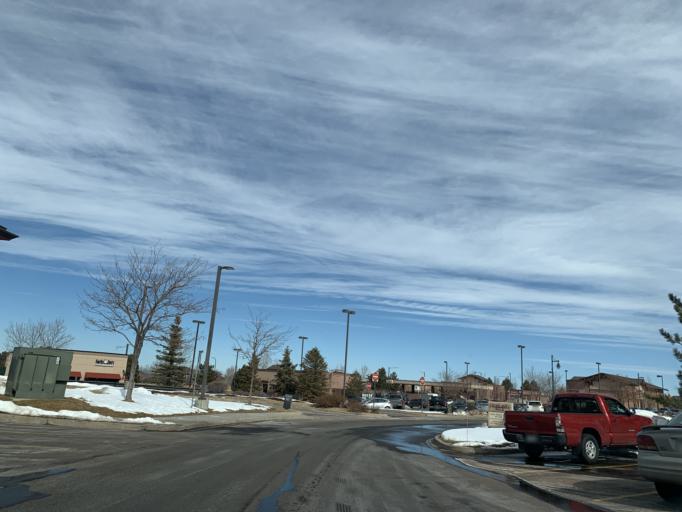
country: US
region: Colorado
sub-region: Douglas County
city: Highlands Ranch
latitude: 39.5252
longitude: -104.9415
